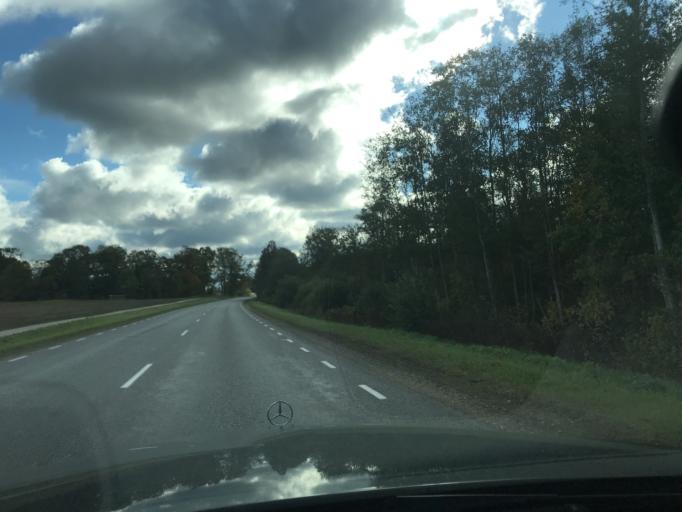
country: EE
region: Vorumaa
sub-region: Antsla vald
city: Vana-Antsla
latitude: 57.9419
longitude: 26.3057
